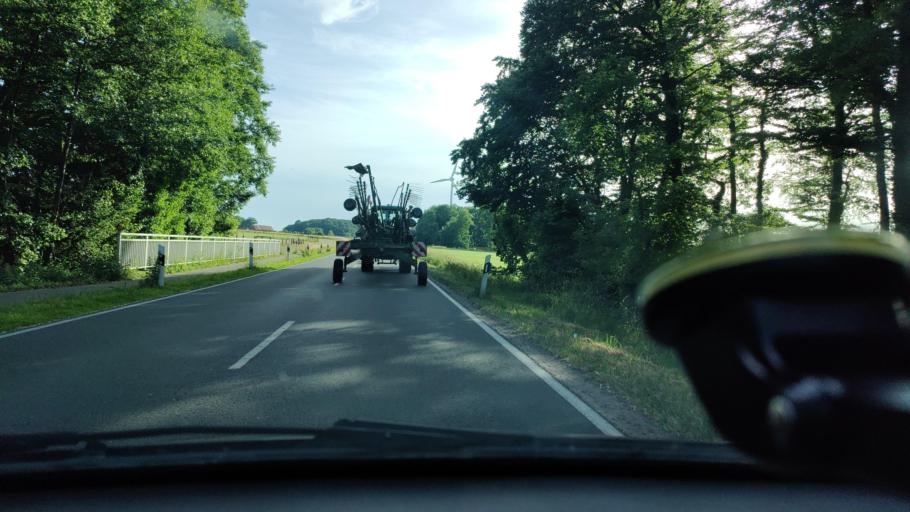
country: DE
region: North Rhine-Westphalia
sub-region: Regierungsbezirk Munster
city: Coesfeld
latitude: 52.0239
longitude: 7.1835
